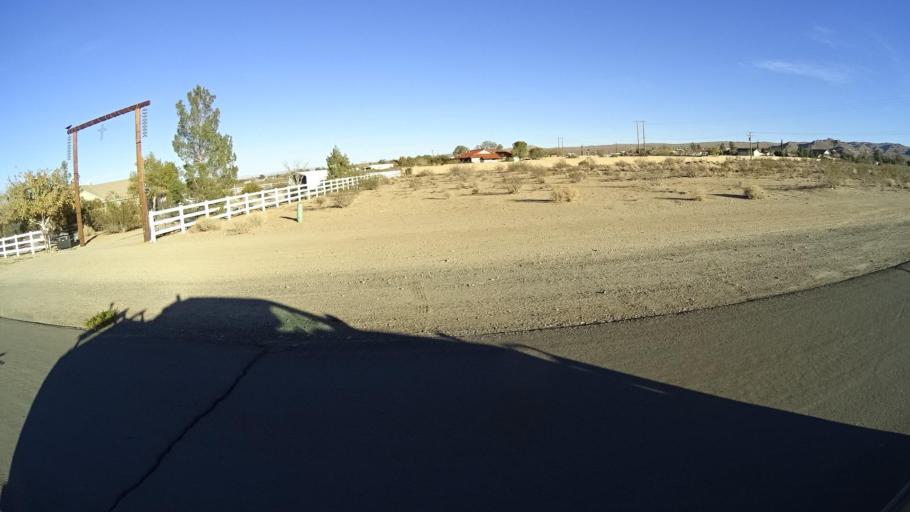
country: US
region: California
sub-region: Kern County
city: Ridgecrest
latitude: 35.5941
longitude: -117.6618
